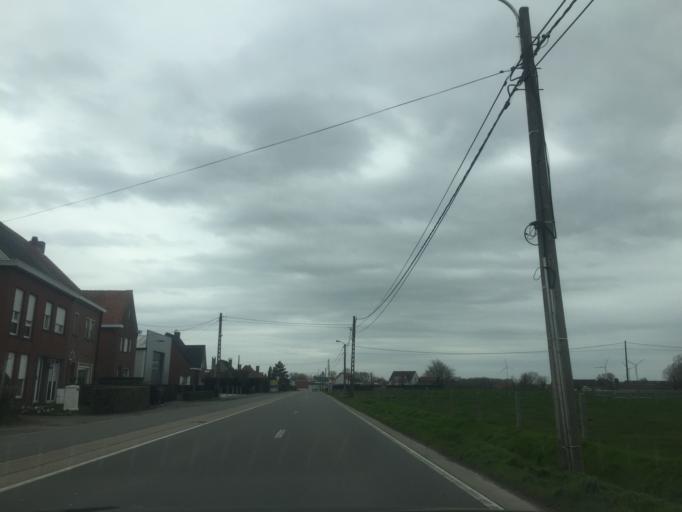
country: BE
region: Flanders
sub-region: Provincie West-Vlaanderen
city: Ardooie
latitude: 50.9614
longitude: 3.1953
